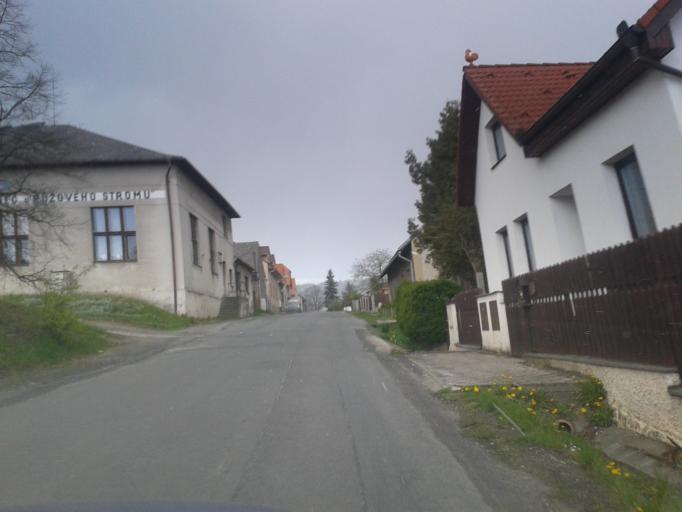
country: CZ
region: Central Bohemia
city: Hudlice
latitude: 49.9621
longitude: 13.9676
